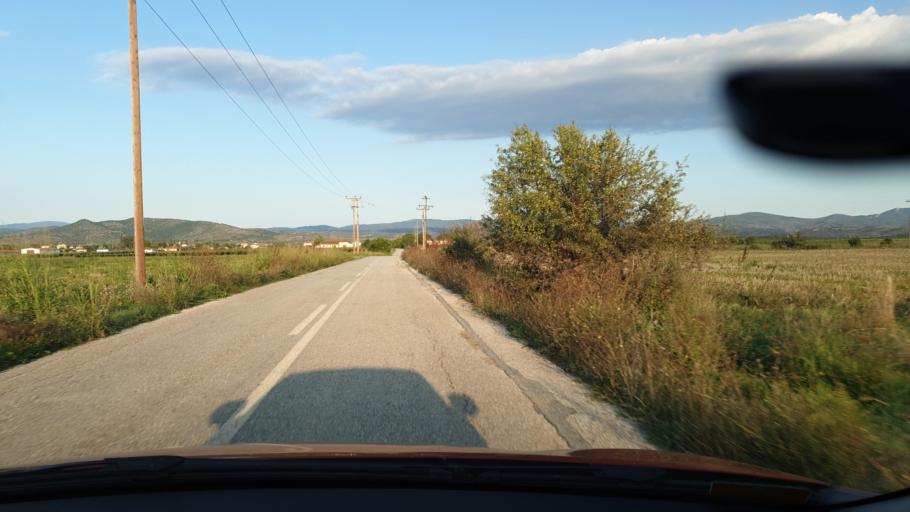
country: GR
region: Central Macedonia
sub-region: Nomos Thessalonikis
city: Nea Apollonia
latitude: 40.5558
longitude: 23.4590
